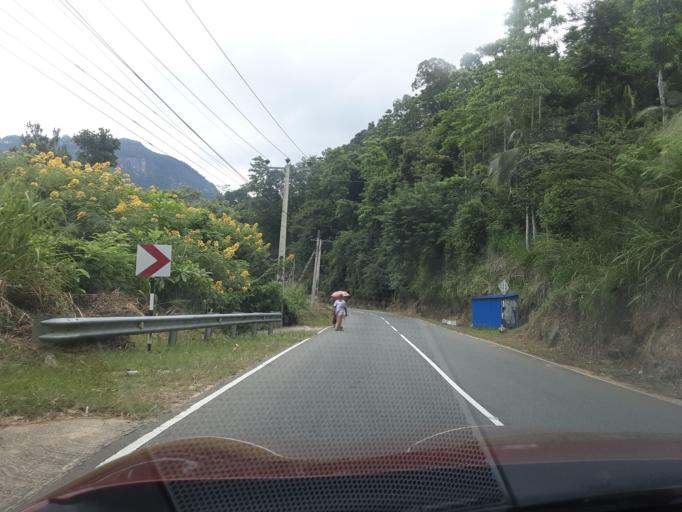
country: LK
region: Uva
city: Badulla
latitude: 6.9332
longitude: 81.1956
